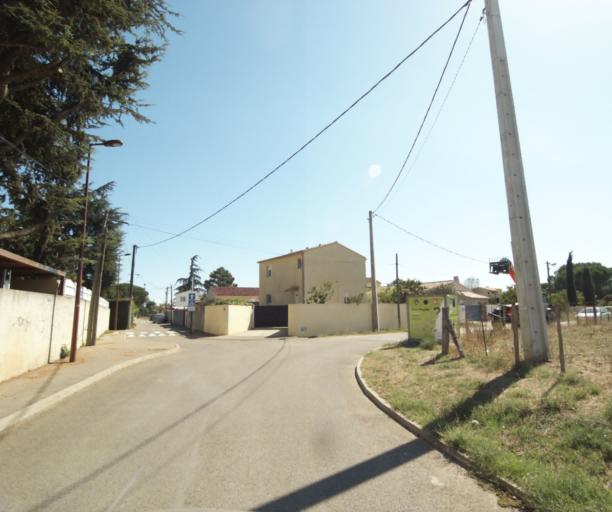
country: FR
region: Languedoc-Roussillon
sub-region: Departement du Gard
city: Rodilhan
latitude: 43.8217
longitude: 4.4301
